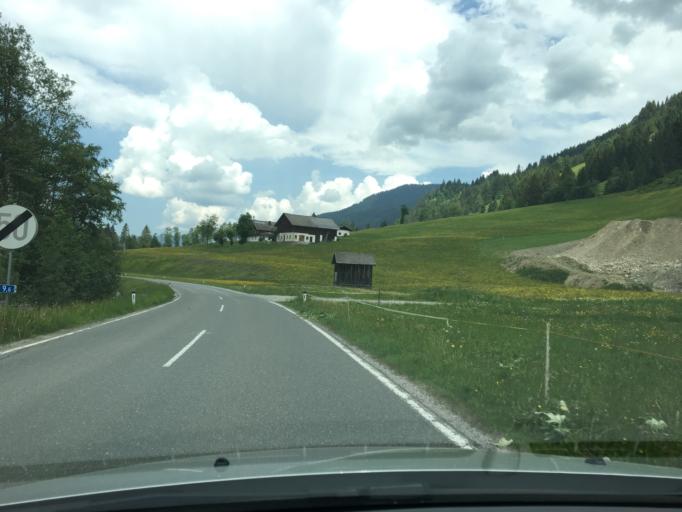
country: AT
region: Salzburg
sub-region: Politischer Bezirk Sankt Johann im Pongau
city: Kleinarl
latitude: 47.2574
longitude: 13.3269
